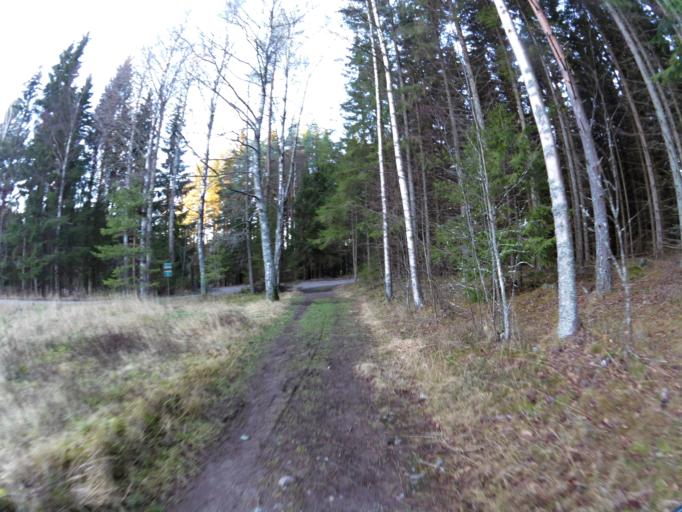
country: NO
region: Ostfold
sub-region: Fredrikstad
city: Fredrikstad
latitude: 59.2450
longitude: 10.9618
